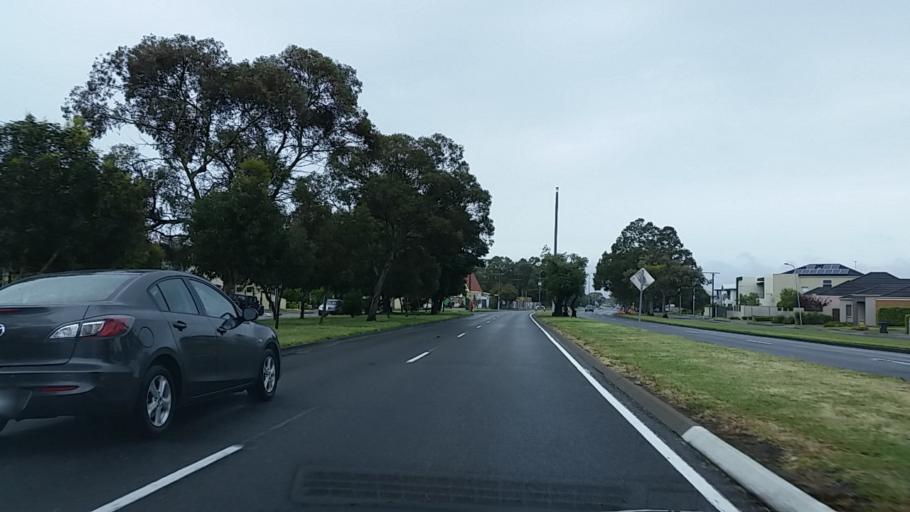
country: AU
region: South Australia
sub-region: Charles Sturt
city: Henley Beach
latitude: -34.9362
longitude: 138.5064
